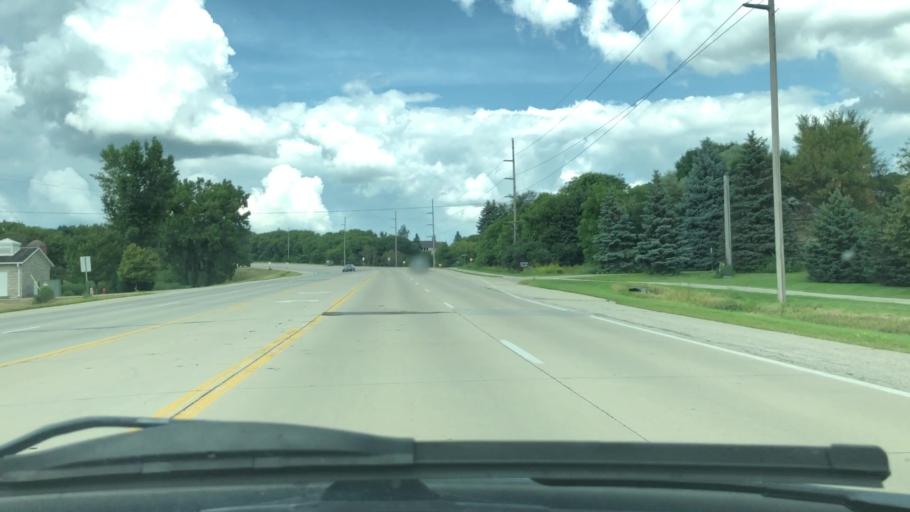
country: US
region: Minnesota
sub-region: Olmsted County
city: Rochester
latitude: 44.0067
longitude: -92.5087
